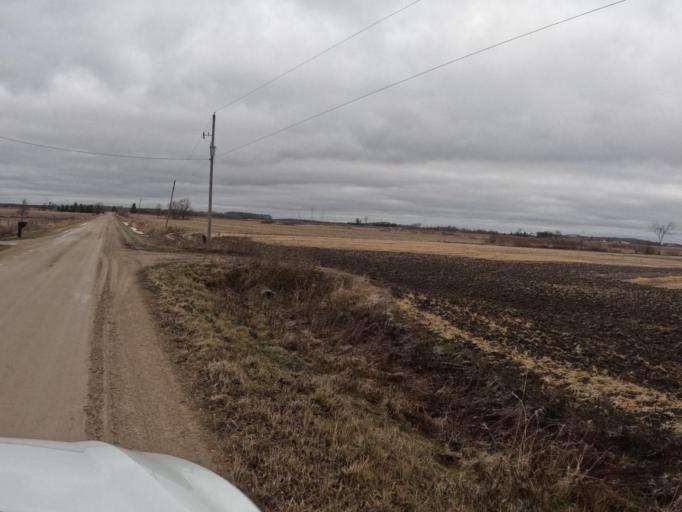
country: CA
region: Ontario
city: Shelburne
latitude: 44.0329
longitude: -80.3717
